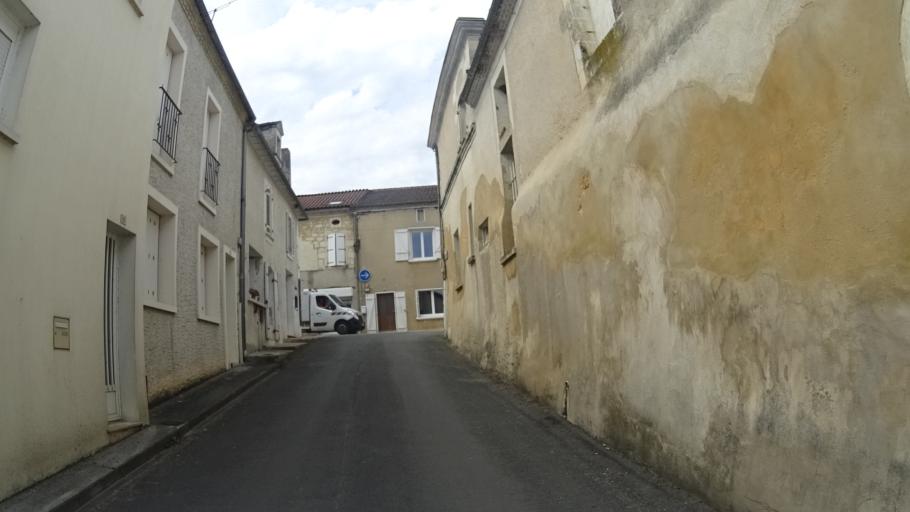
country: FR
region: Aquitaine
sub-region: Departement de la Dordogne
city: Neuvic
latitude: 45.0201
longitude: 0.5380
